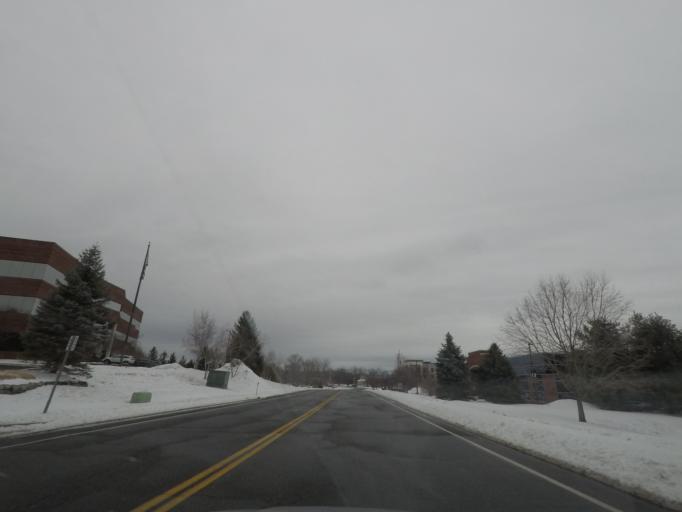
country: US
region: New York
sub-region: Schenectady County
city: Niskayuna
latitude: 42.7680
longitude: -73.8226
